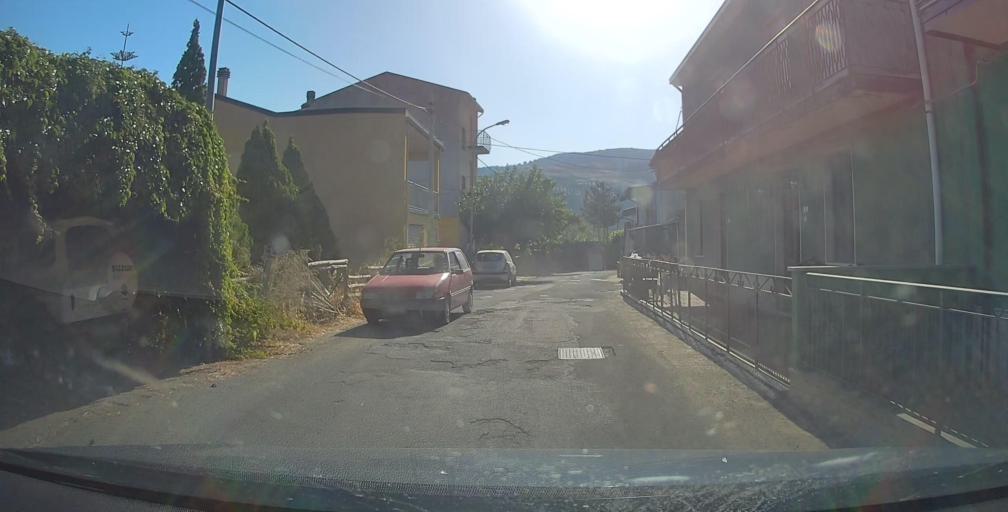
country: IT
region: Sicily
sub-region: Messina
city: San Piero Patti
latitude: 38.0751
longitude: 14.9836
